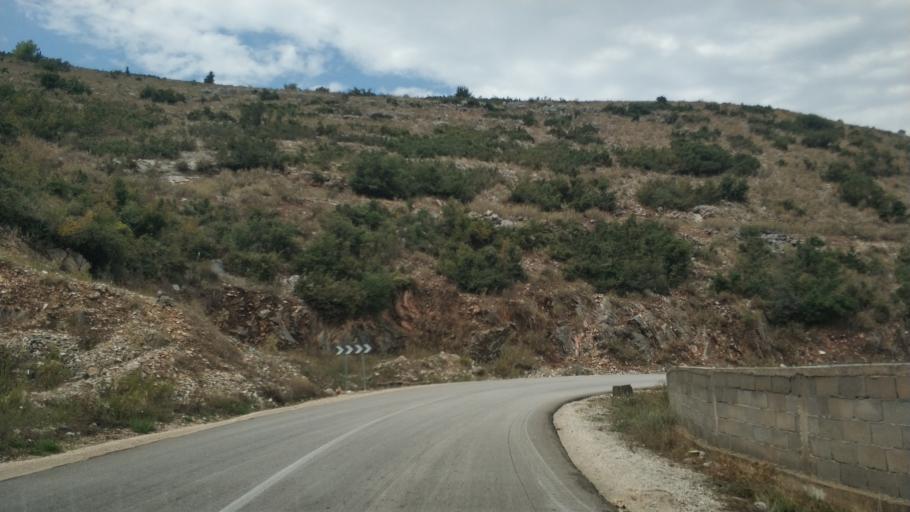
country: AL
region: Vlore
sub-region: Rrethi i Sarandes
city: Sarande
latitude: 39.8547
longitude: 20.0350
